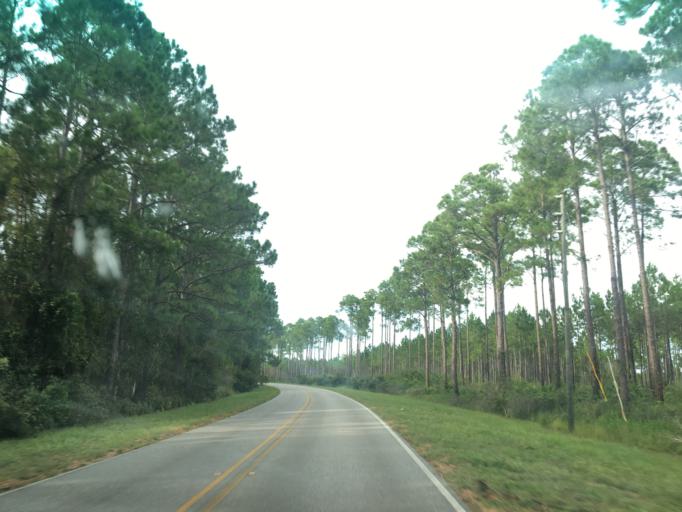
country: US
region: Florida
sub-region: Wakulla County
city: Crawfordville
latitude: 29.9324
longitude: -84.3785
